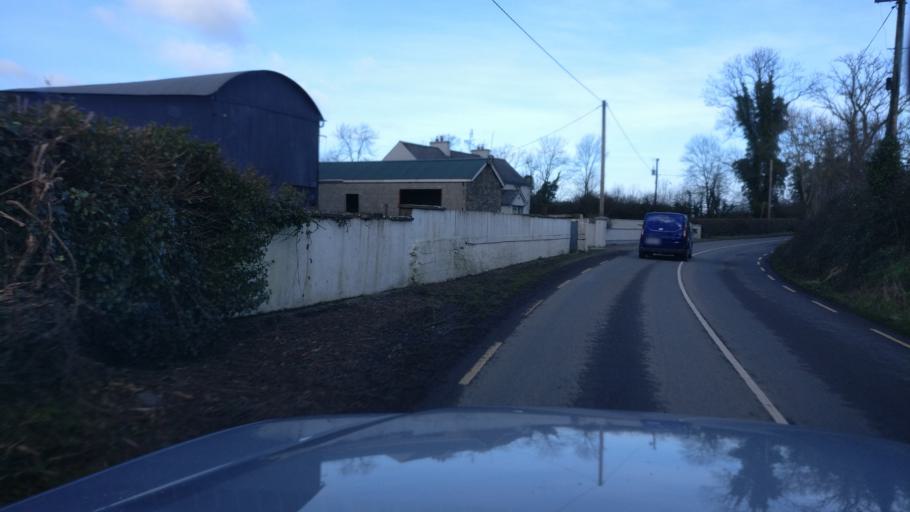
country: IE
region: Leinster
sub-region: Kilkenny
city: Castlecomer
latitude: 52.8427
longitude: -7.1852
